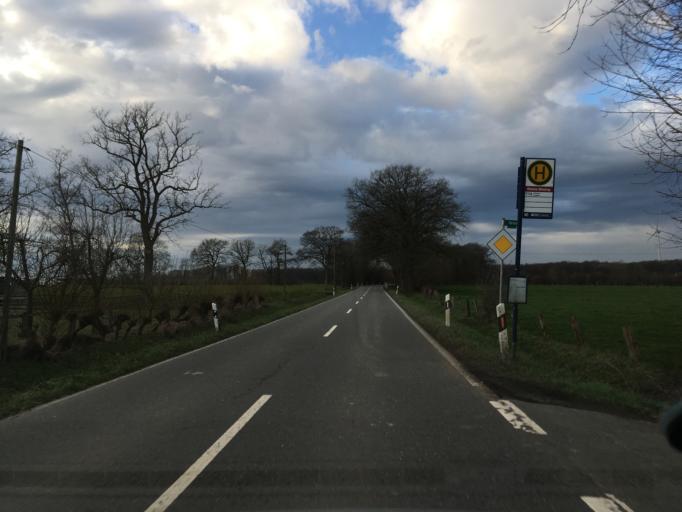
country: DE
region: North Rhine-Westphalia
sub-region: Regierungsbezirk Munster
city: Schoppingen
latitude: 52.0497
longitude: 7.2019
